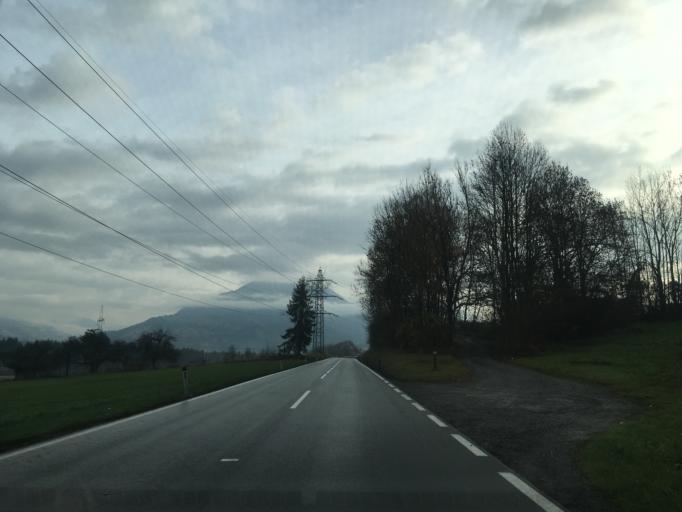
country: AT
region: Vorarlberg
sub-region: Politischer Bezirk Bludenz
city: Nenzing
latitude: 47.1792
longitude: 9.7195
